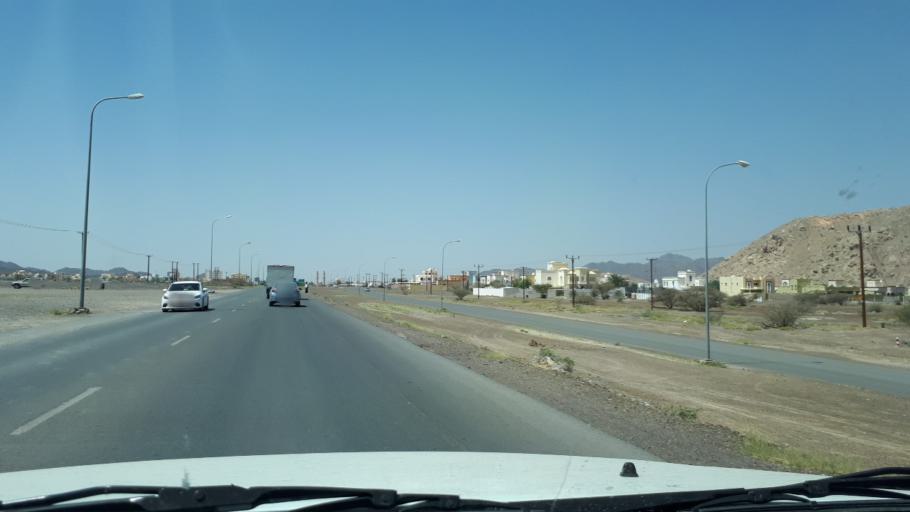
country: OM
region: Muhafazat ad Dakhiliyah
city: Bahla'
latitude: 23.0098
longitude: 57.3239
